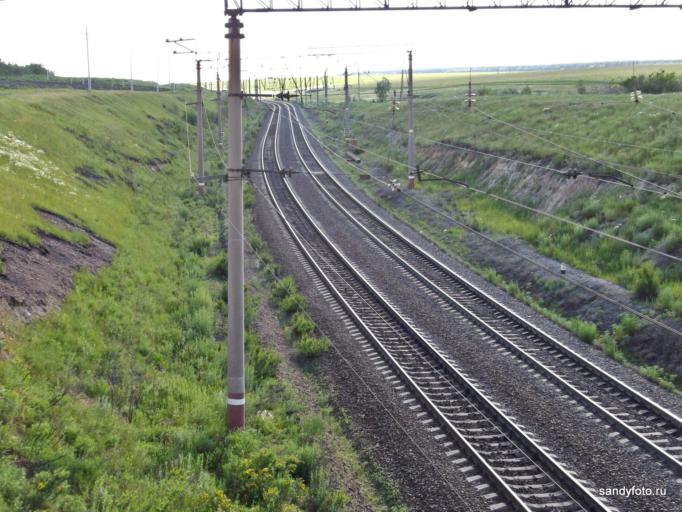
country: RU
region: Chelyabinsk
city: Troitsk
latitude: 54.0370
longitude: 61.6053
